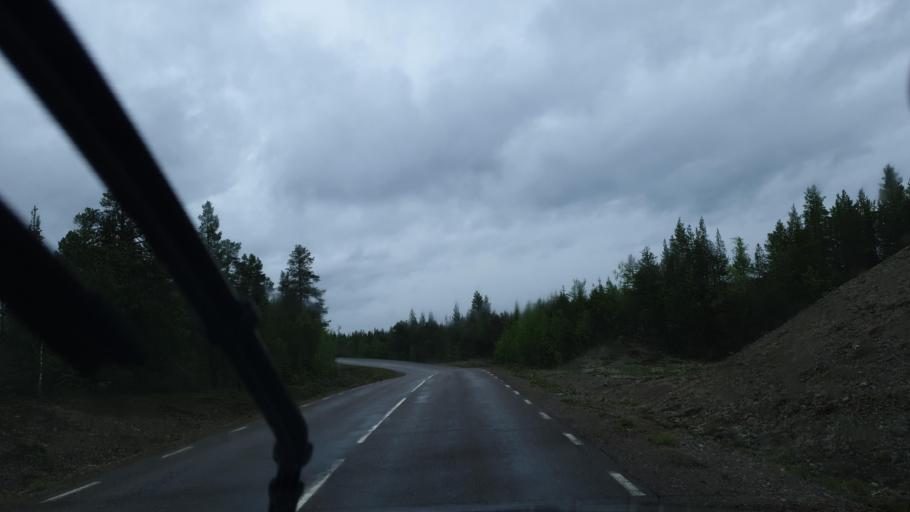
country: SE
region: Norrbotten
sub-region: Kiruna Kommun
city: Kiruna
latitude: 67.8723
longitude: 20.9870
